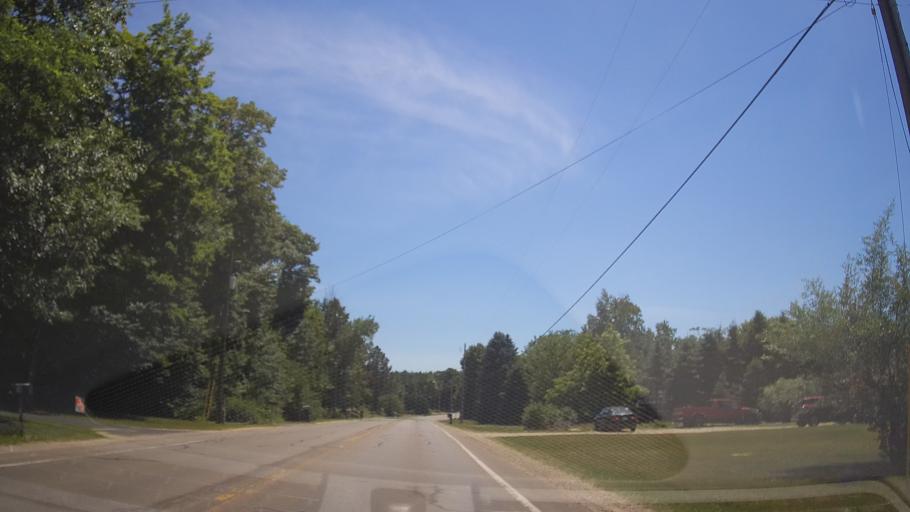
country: US
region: Michigan
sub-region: Grand Traverse County
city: Traverse City
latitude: 44.6887
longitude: -85.6900
